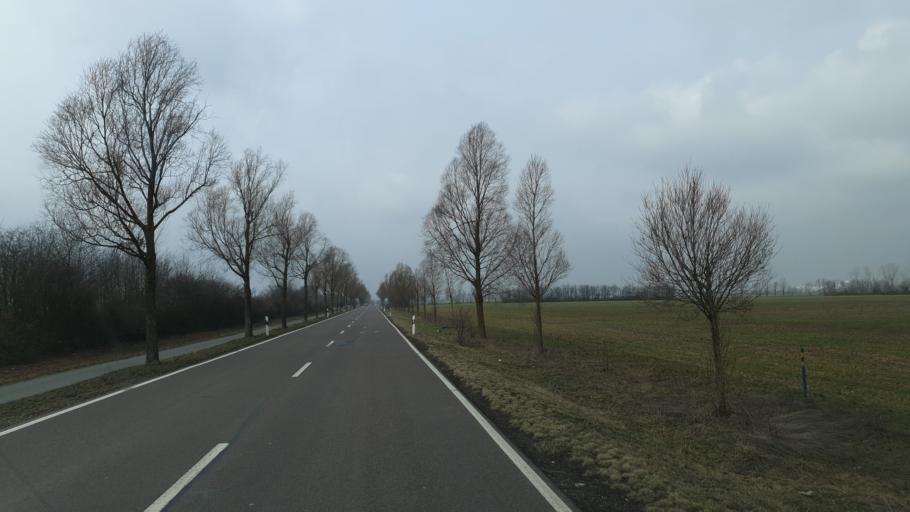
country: DE
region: Saxony
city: Zwochau
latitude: 51.4368
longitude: 12.2656
